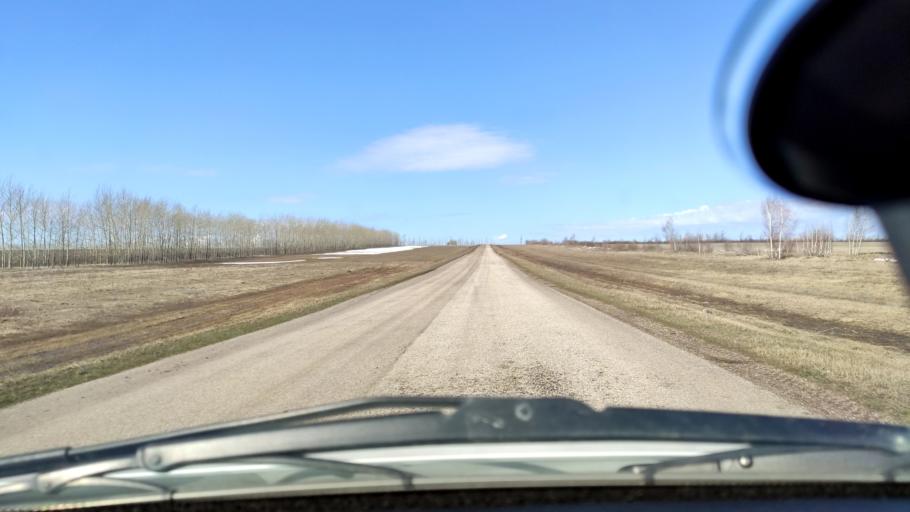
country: RU
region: Bashkortostan
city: Tolbazy
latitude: 54.1709
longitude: 55.9127
